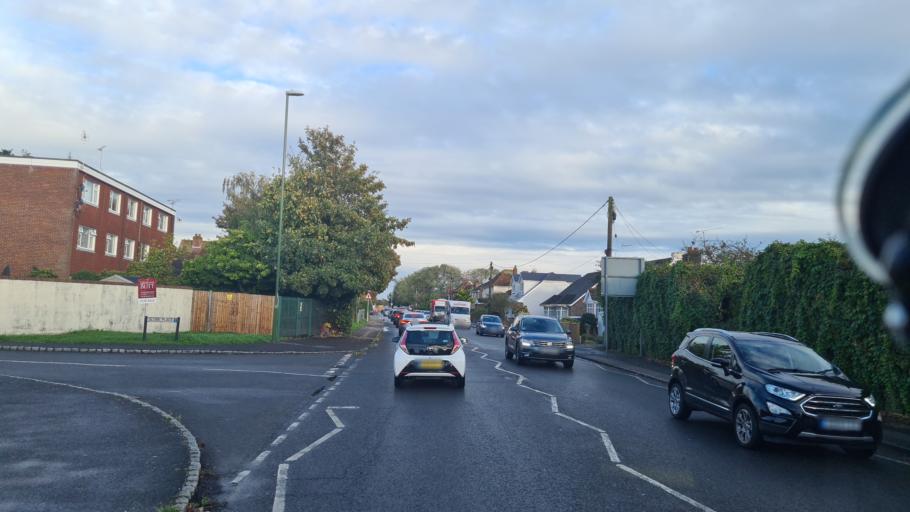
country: GB
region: England
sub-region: West Sussex
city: Littlehampton
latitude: 50.8213
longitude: -0.5431
